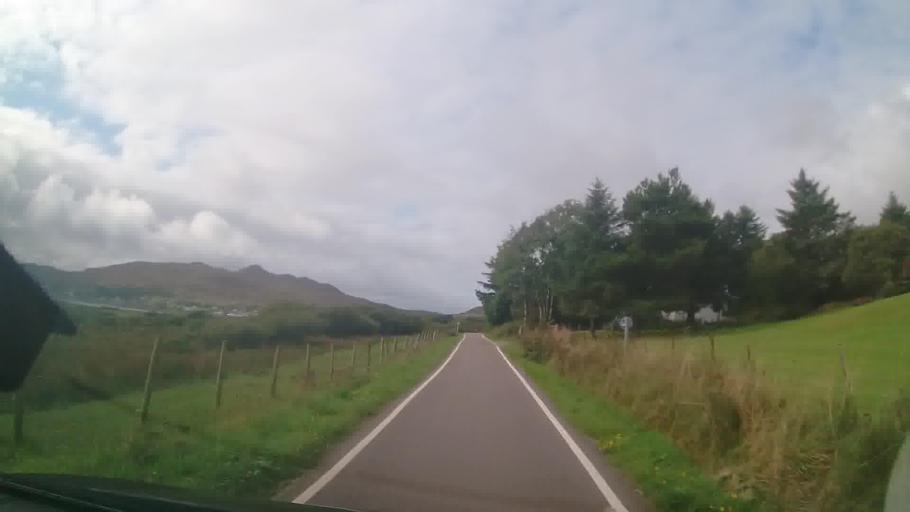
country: GB
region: Scotland
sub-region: Argyll and Bute
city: Isle Of Mull
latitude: 56.6945
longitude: -6.0973
